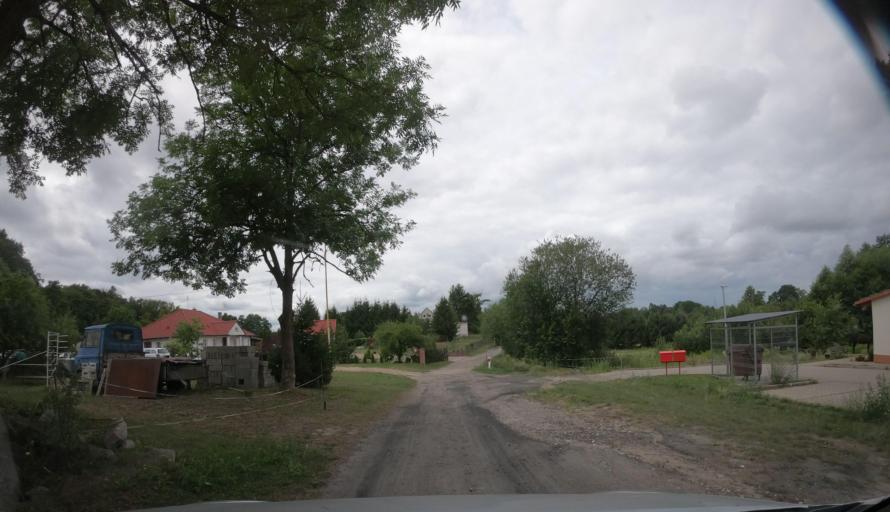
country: PL
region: West Pomeranian Voivodeship
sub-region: Powiat kamienski
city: Golczewo
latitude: 53.8163
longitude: 14.9874
